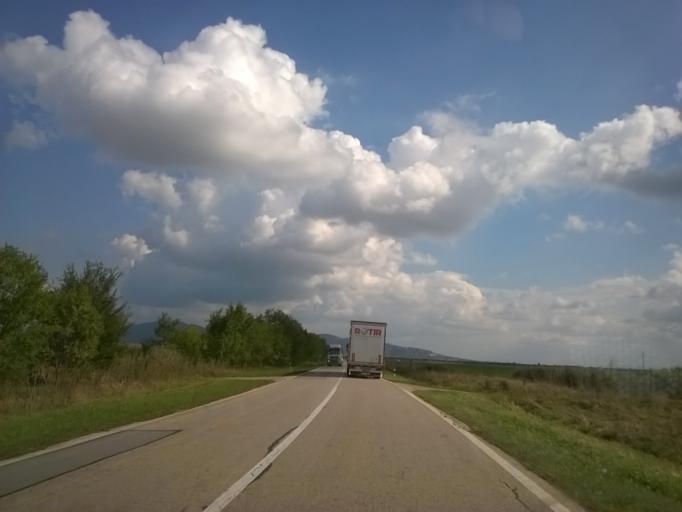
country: RS
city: Pavlis
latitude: 45.1590
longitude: 21.2420
